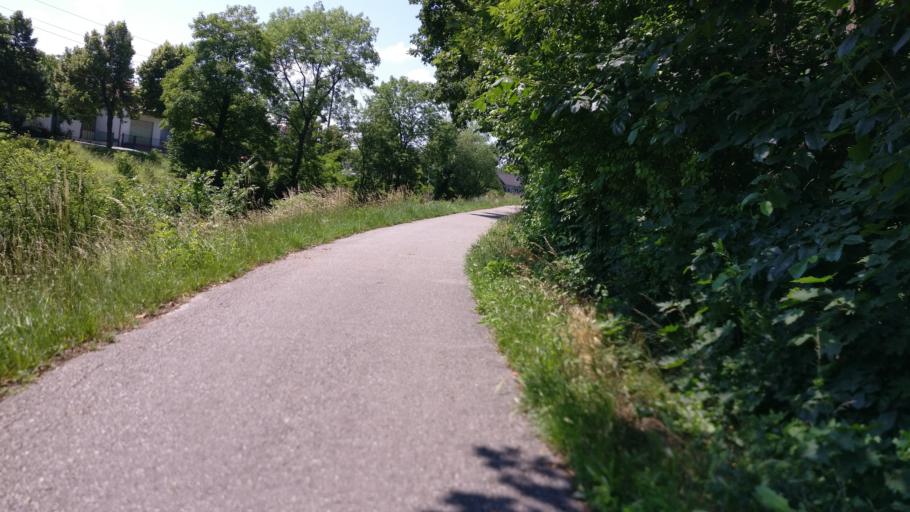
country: AT
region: Lower Austria
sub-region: Politischer Bezirk Baden
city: Oberwaltersdorf
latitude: 47.9723
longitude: 16.3211
